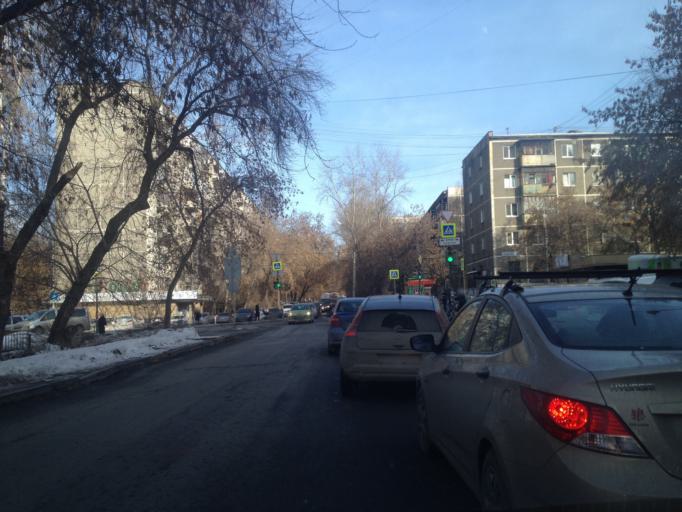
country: RU
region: Sverdlovsk
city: Yekaterinburg
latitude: 56.8323
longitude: 60.6284
